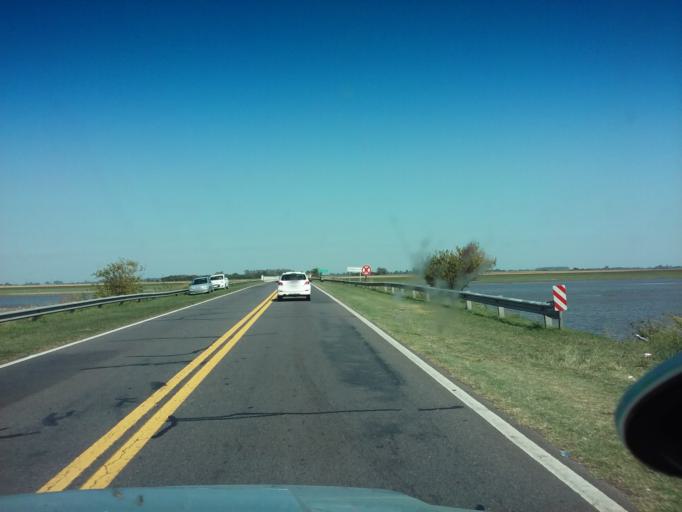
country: AR
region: Buenos Aires
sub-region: Partido de Alberti
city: Alberti
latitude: -35.0623
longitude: -60.2911
